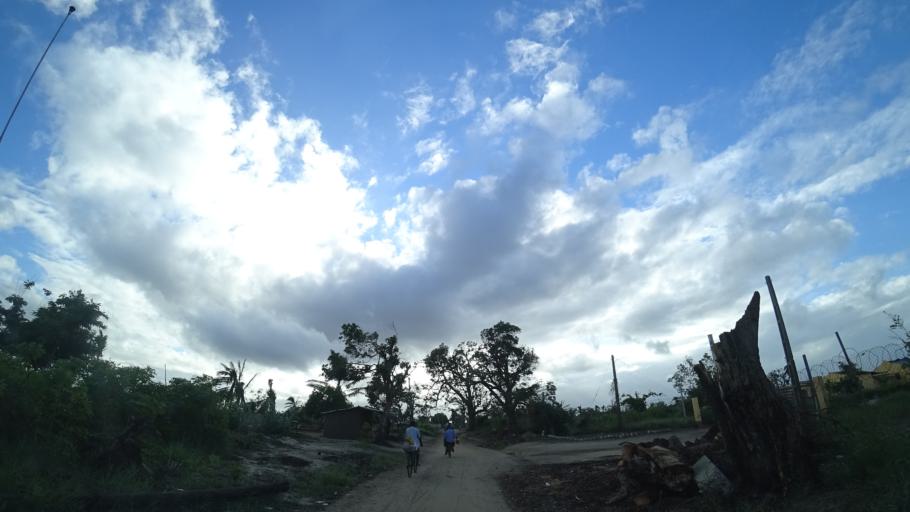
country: MZ
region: Sofala
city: Beira
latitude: -19.7149
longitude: 35.0094
